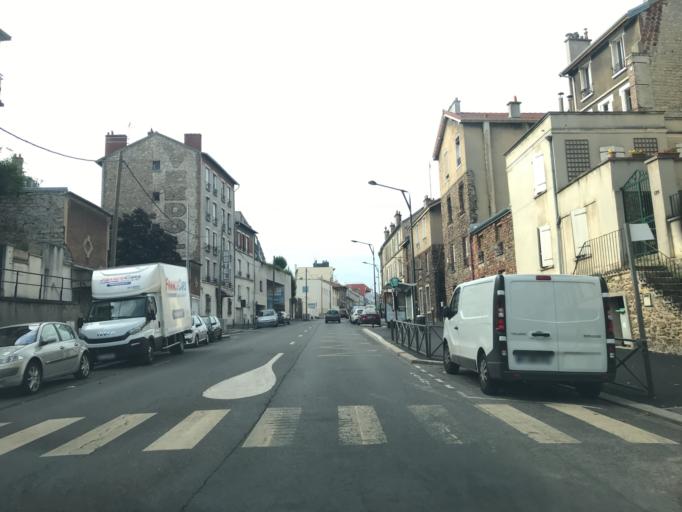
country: FR
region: Ile-de-France
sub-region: Departement du Val-de-Marne
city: Villejuif
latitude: 48.7980
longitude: 2.3660
